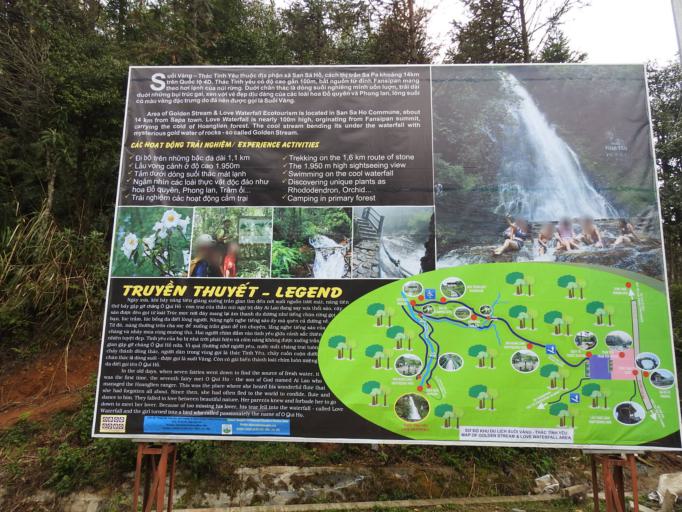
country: VN
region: Lao Cai
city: Sa Pa
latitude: 22.3525
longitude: 103.7744
